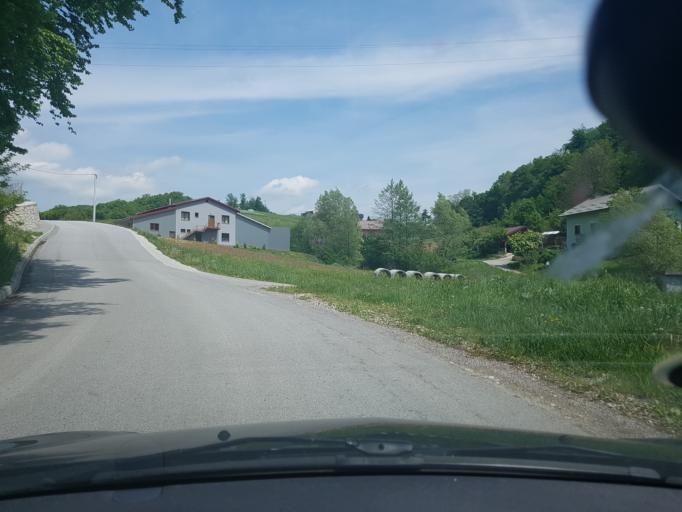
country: HR
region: Krapinsko-Zagorska
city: Pregrada
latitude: 46.2019
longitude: 15.7324
